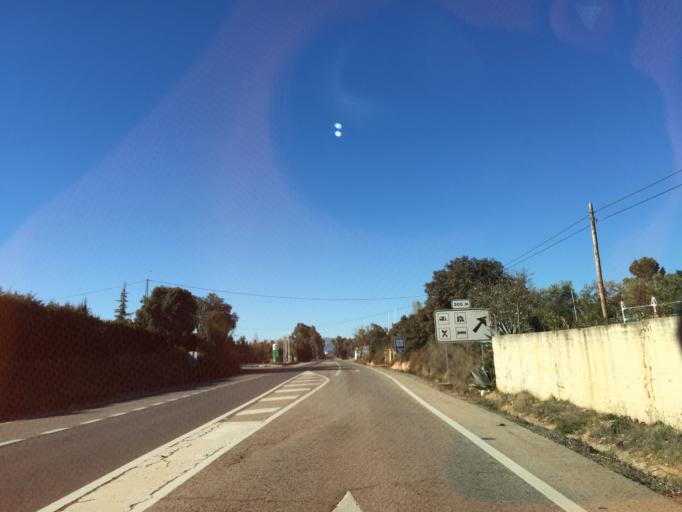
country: ES
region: Andalusia
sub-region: Provincia de Malaga
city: Arriate
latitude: 36.7848
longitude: -5.1147
